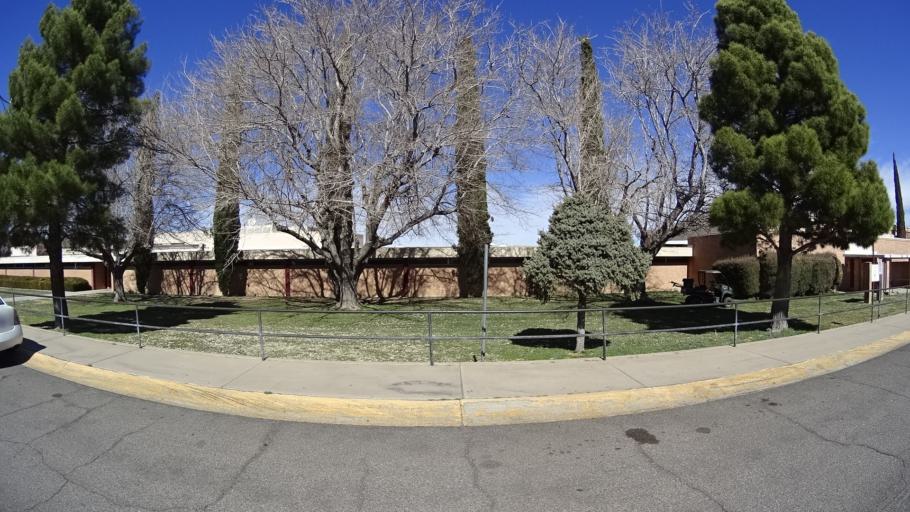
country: US
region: Arizona
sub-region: Mohave County
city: Kingman
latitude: 35.2140
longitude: -114.0326
